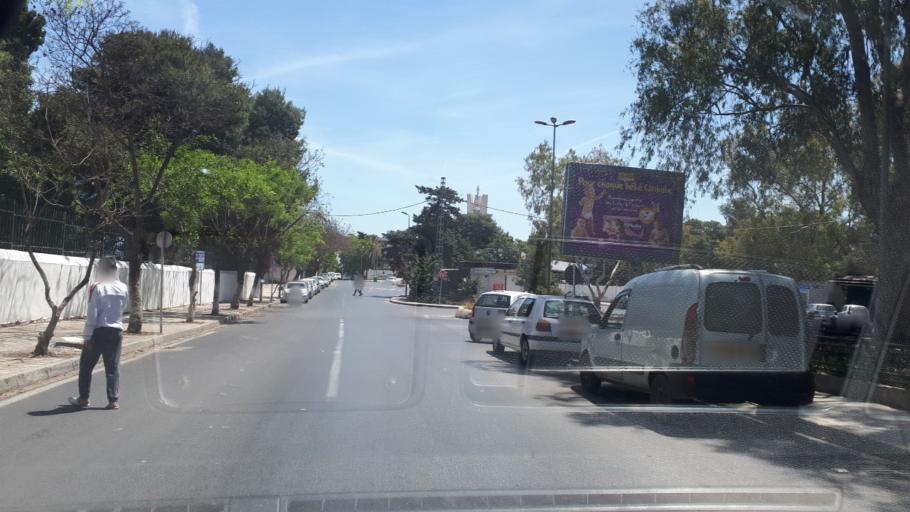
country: DZ
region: Alger
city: Algiers
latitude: 36.7475
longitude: 3.0609
